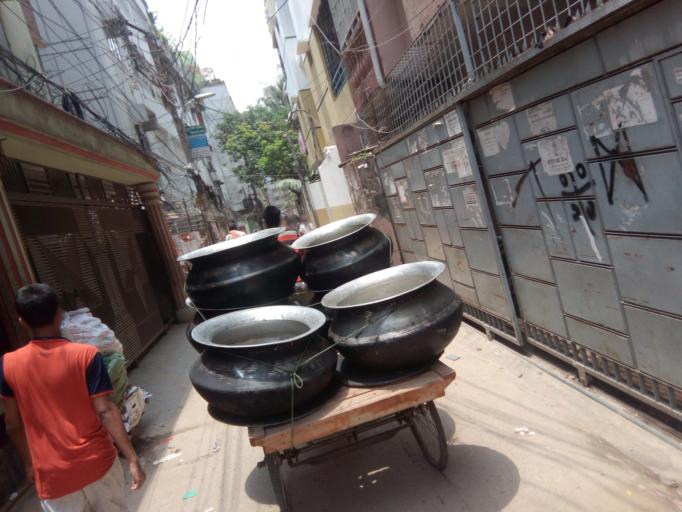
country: BD
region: Dhaka
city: Paltan
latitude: 23.7405
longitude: 90.4152
